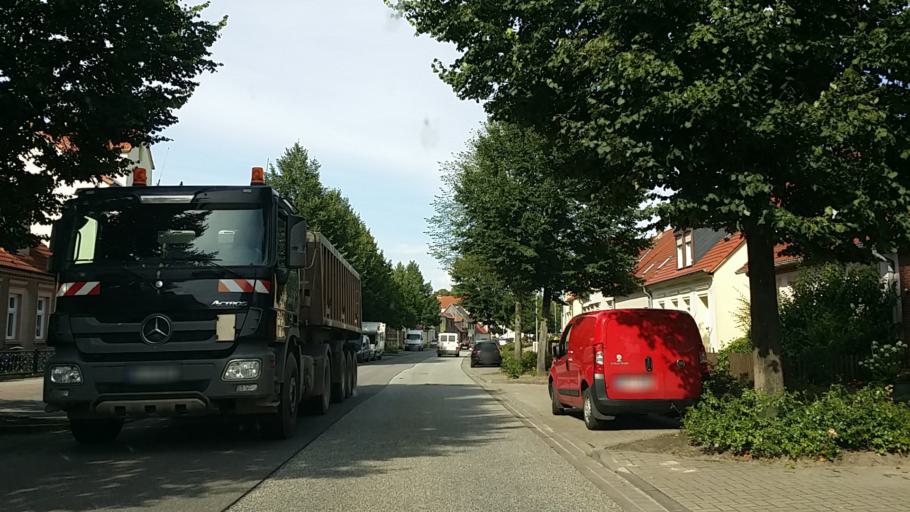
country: DE
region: Brandenburg
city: Perleberg
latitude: 53.0707
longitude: 11.8600
